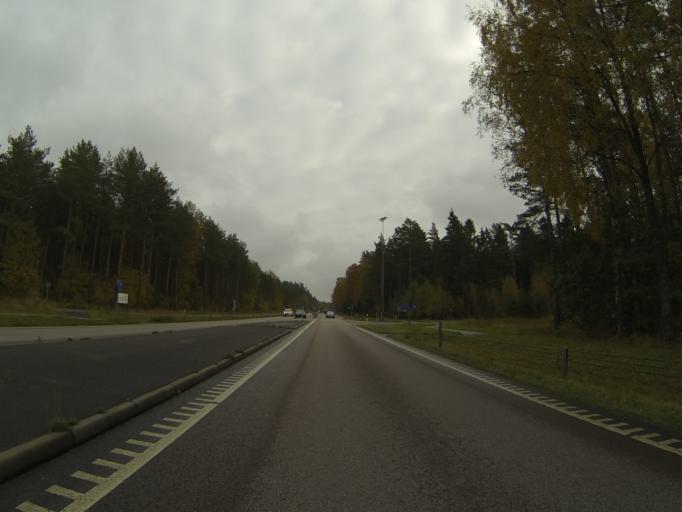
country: SE
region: Skane
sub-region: Sjobo Kommun
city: Sjoebo
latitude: 55.6374
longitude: 13.6537
